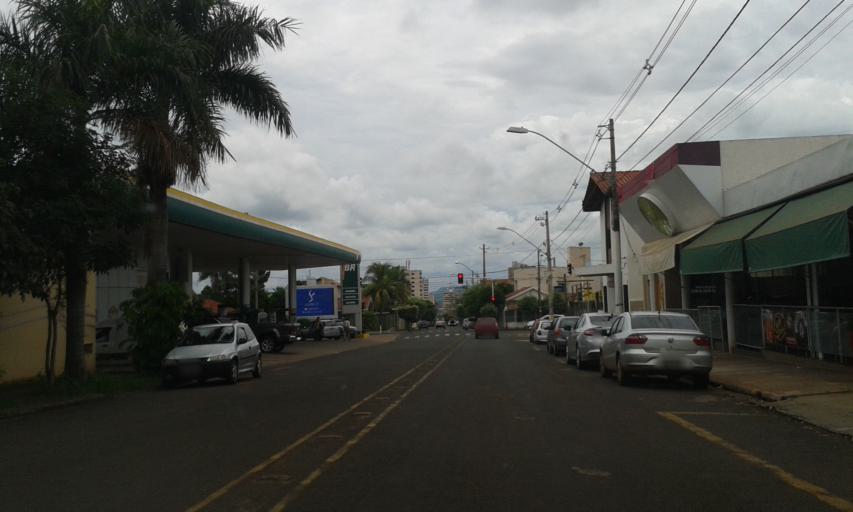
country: BR
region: Minas Gerais
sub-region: Ituiutaba
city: Ituiutaba
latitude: -18.9832
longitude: -49.4599
